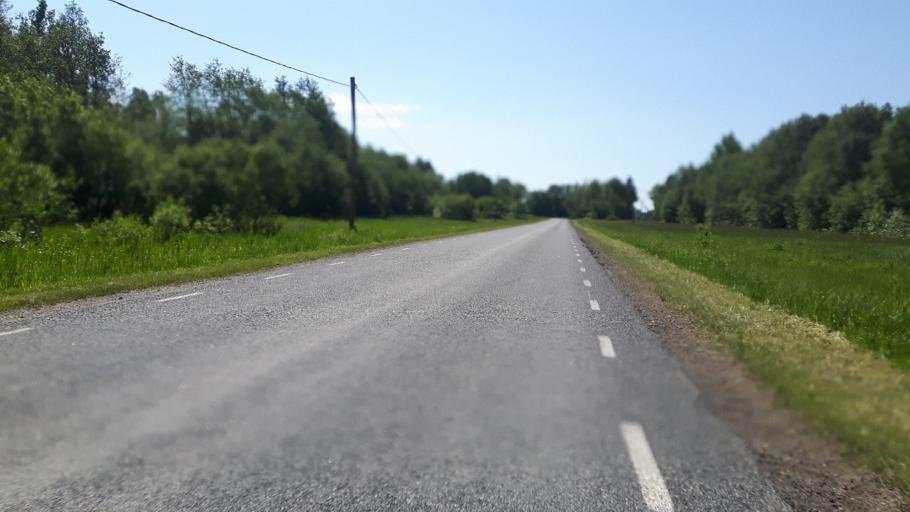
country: EE
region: Paernumaa
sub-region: Vaendra vald (alev)
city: Vandra
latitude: 58.6013
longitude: 25.0221
